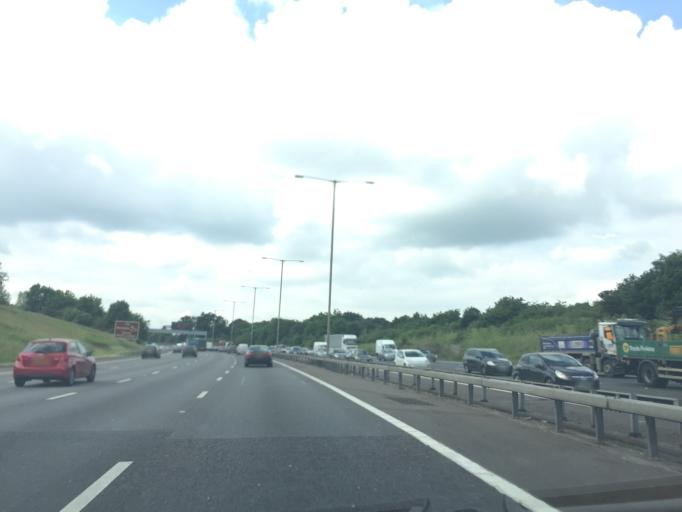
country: GB
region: England
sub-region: Buckinghamshire
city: Denham
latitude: 51.5439
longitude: -0.5060
